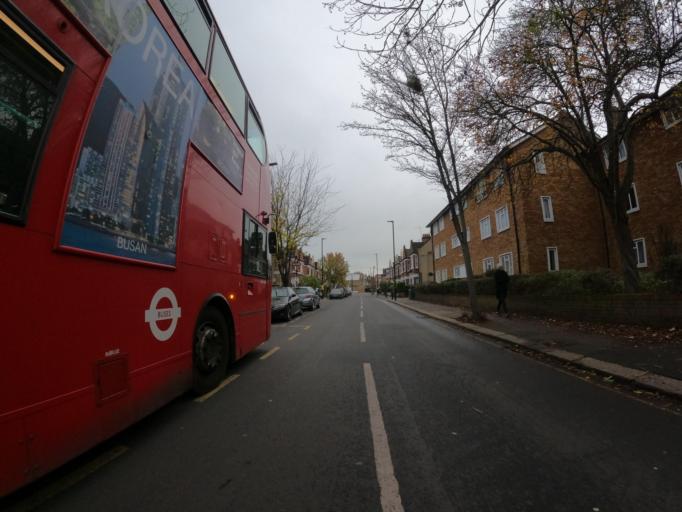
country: GB
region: England
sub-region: Greater London
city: Acton
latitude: 51.5024
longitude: -0.2578
